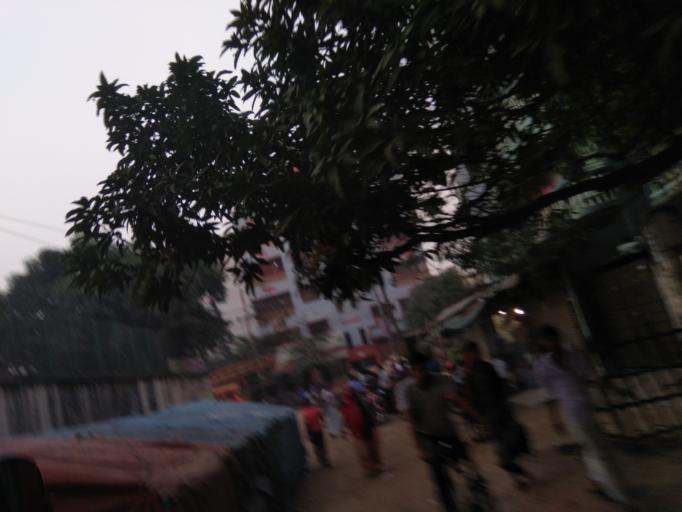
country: BD
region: Dhaka
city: Azimpur
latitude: 23.8097
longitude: 90.3763
